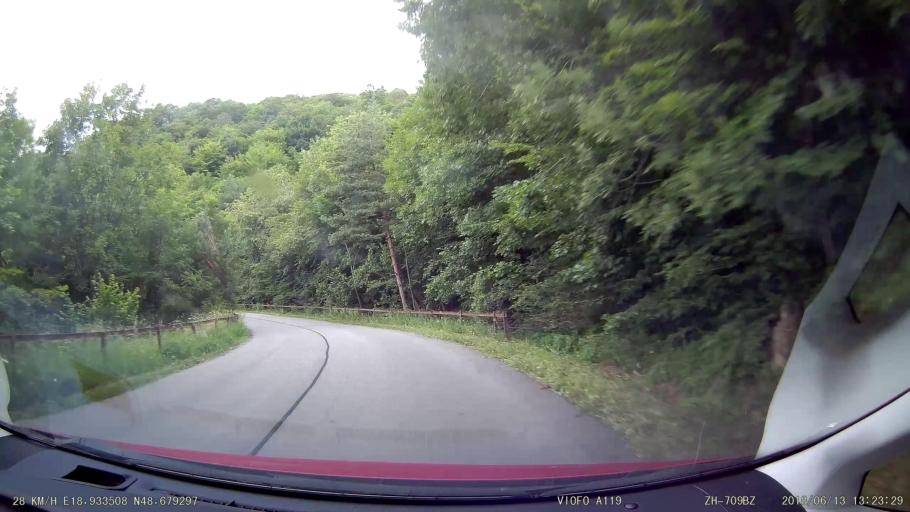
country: SK
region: Banskobystricky
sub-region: Okres Ziar nad Hronom
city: Kremnica
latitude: 48.6798
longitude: 18.9335
